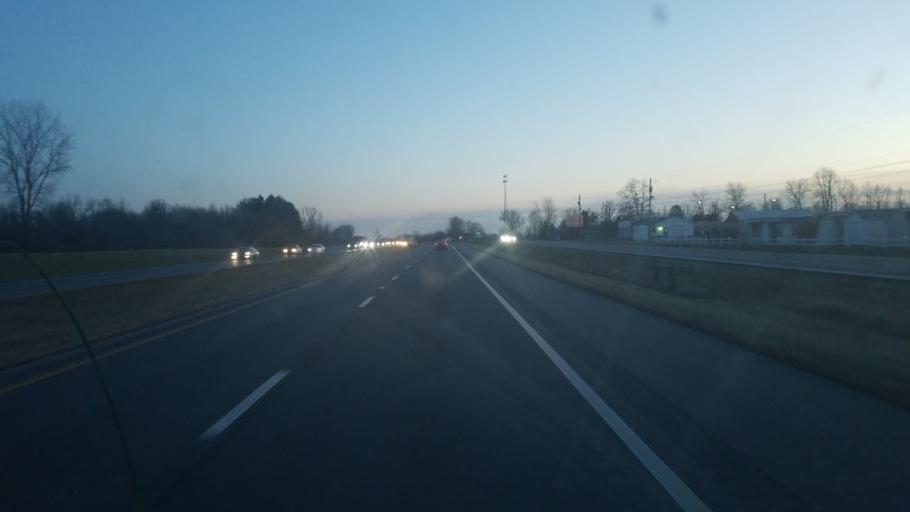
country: US
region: Ohio
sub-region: Marion County
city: Prospect
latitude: 40.4470
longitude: -83.0750
